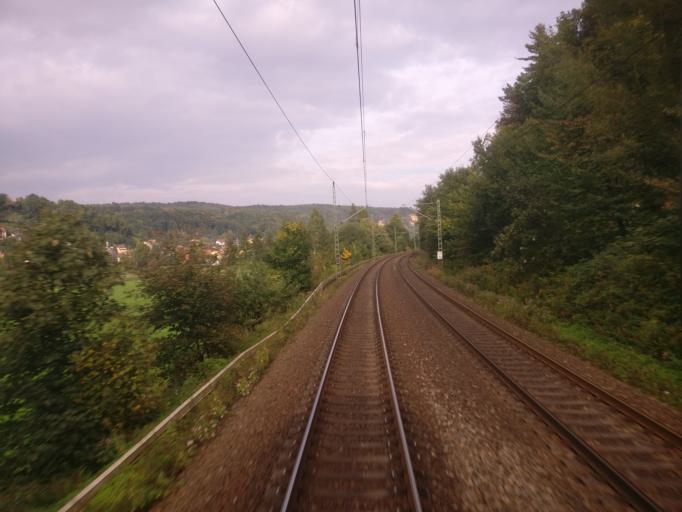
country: DE
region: Saxony
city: Stadt Wehlen
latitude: 50.9521
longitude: 14.0251
